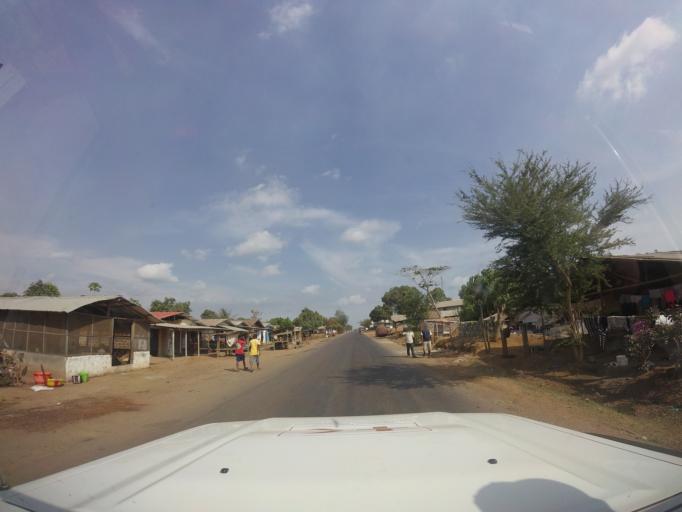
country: LR
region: Bomi
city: Tubmanburg
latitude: 6.7171
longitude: -10.9748
